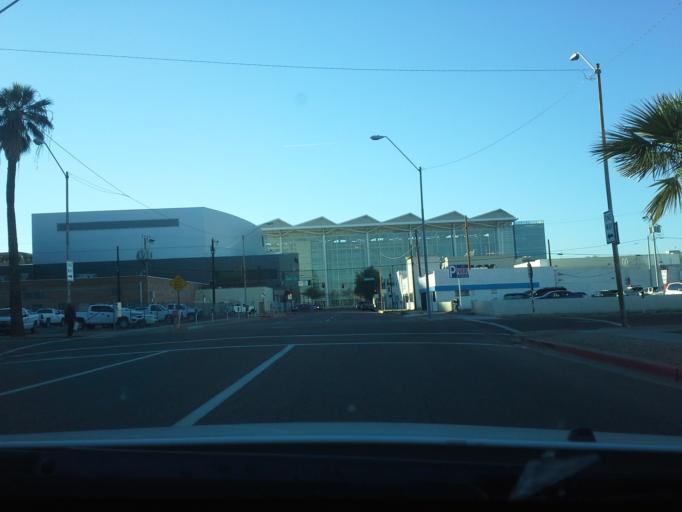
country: US
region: Arizona
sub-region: Maricopa County
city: Phoenix
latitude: 33.4507
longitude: -112.0803
